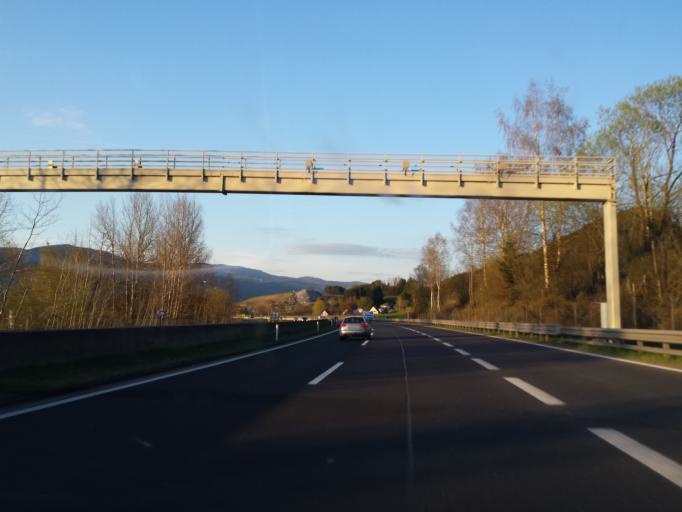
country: AT
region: Styria
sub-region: Politischer Bezirk Bruck-Muerzzuschlag
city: Frauenberg
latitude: 47.4517
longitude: 15.3415
